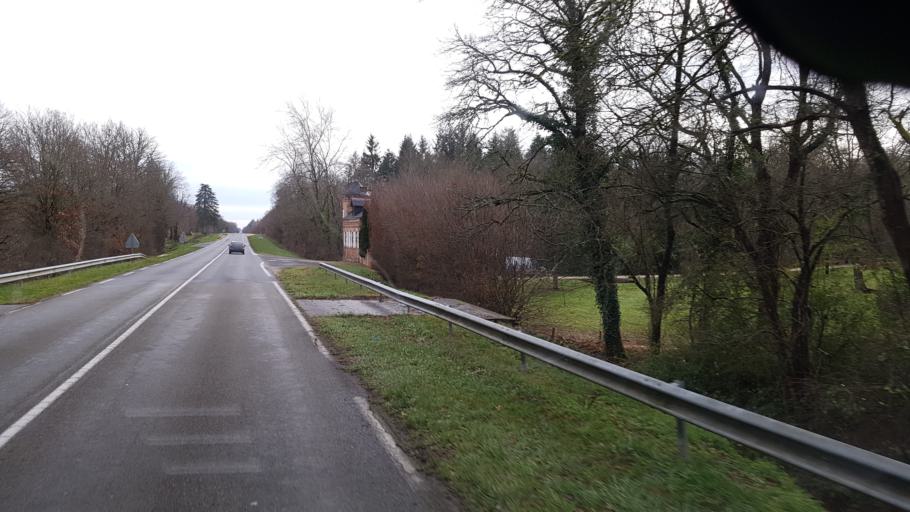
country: FR
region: Centre
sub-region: Departement du Loiret
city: La Ferte-Saint-Aubin
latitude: 47.6883
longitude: 1.9586
